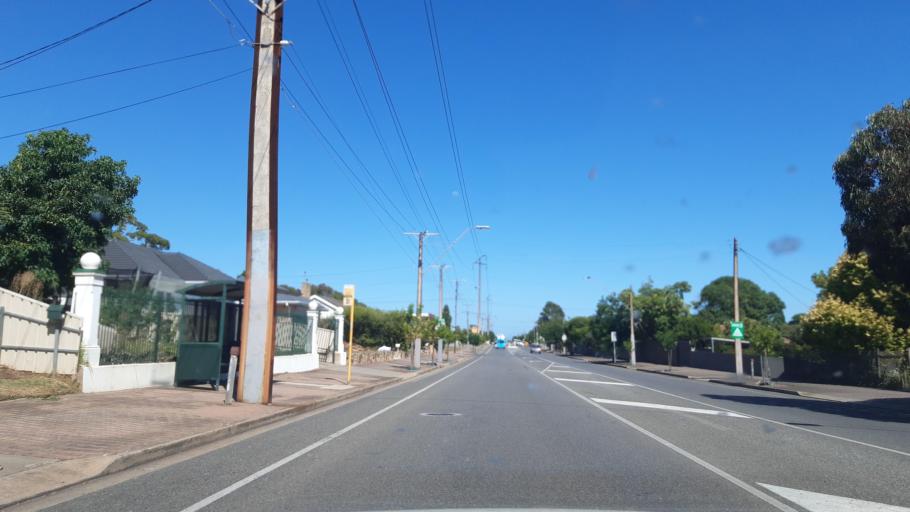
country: AU
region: South Australia
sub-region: Marion
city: Sturt
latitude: -35.0286
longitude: 138.5537
